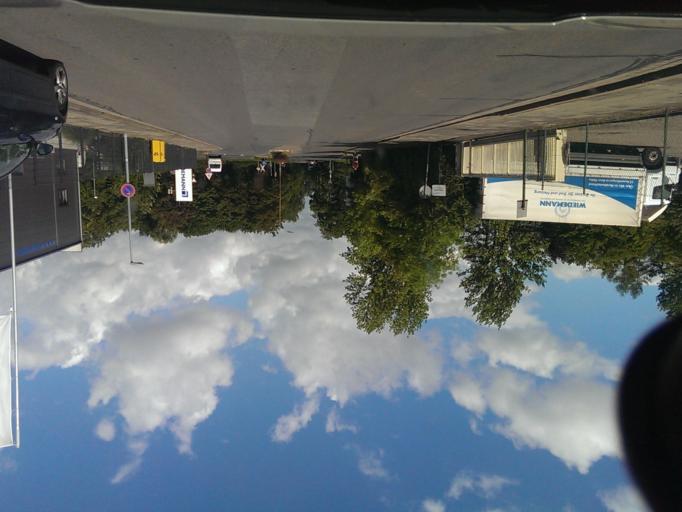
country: DE
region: Lower Saxony
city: Sarstedt
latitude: 52.2486
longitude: 9.8585
